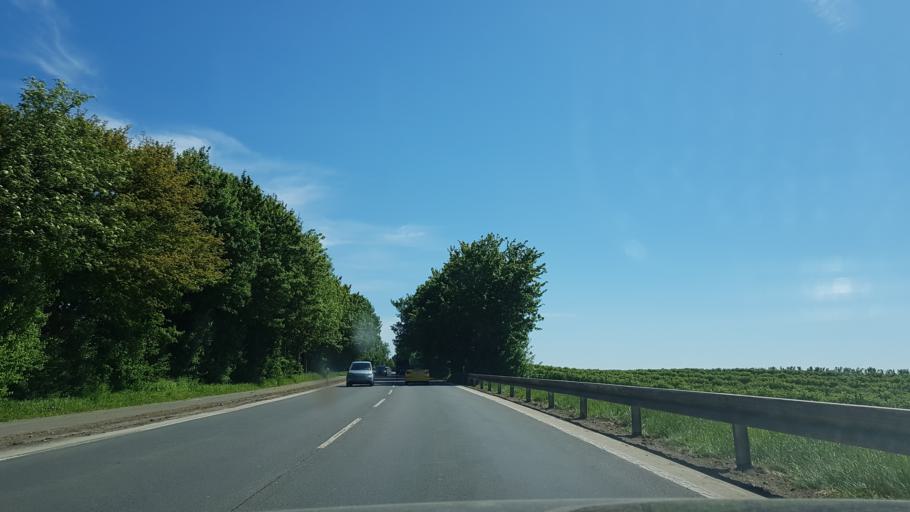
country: DE
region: North Rhine-Westphalia
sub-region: Regierungsbezirk Dusseldorf
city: Ratingen
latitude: 51.2950
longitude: 6.9108
